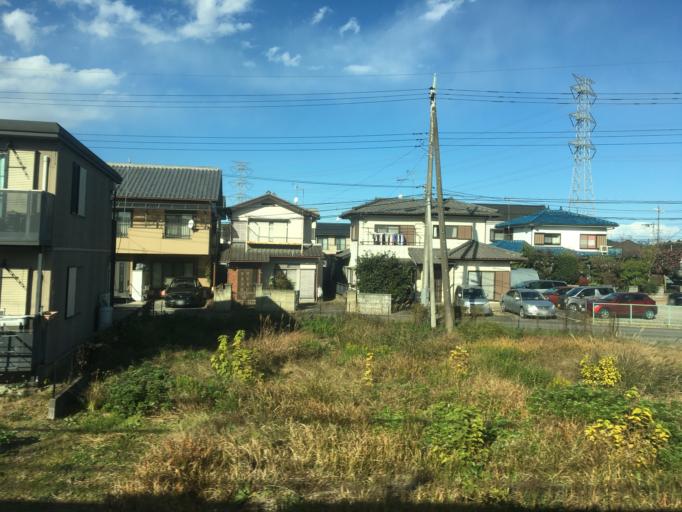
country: JP
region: Saitama
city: Kumagaya
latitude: 36.0474
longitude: 139.3634
